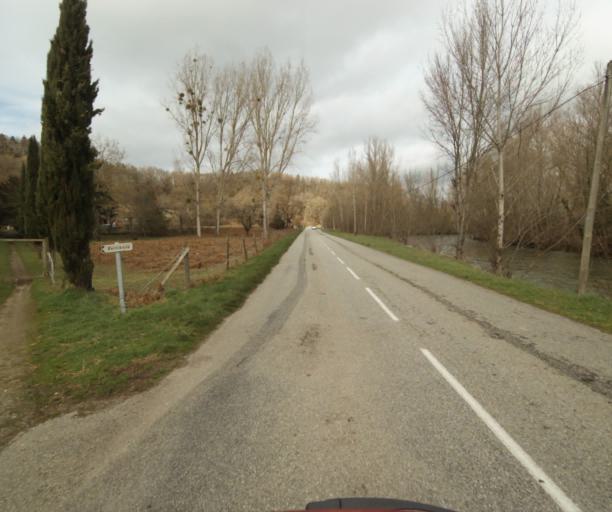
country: FR
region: Midi-Pyrenees
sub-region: Departement de l'Ariege
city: Pamiers
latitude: 43.1435
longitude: 1.5914
